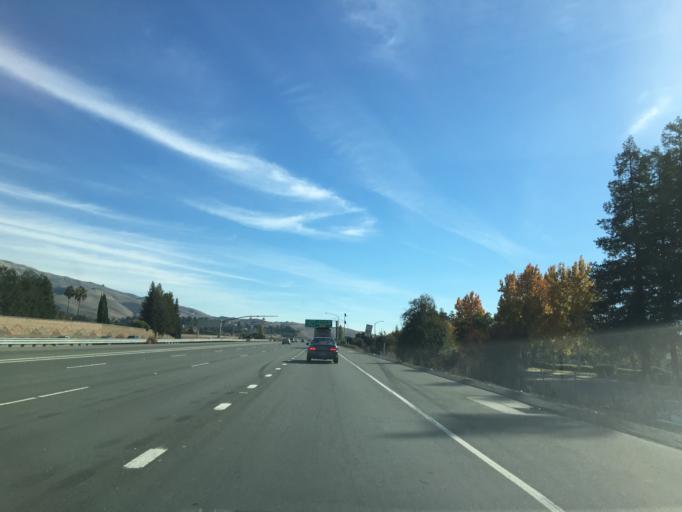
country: US
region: California
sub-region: Alameda County
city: Fremont
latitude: 37.5013
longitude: -121.9300
